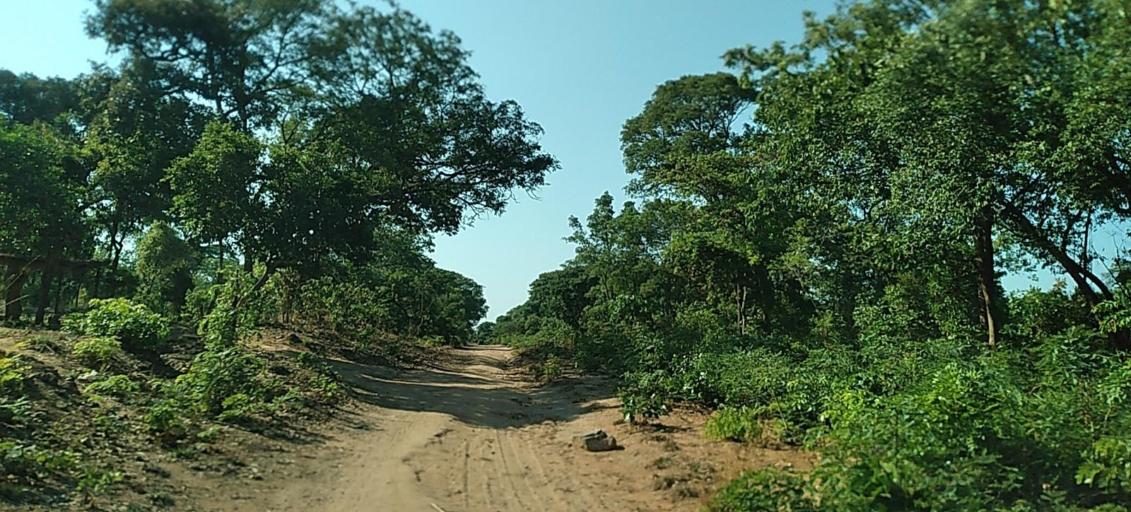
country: ZM
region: Central
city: Mkushi
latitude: -13.4628
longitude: 28.9128
